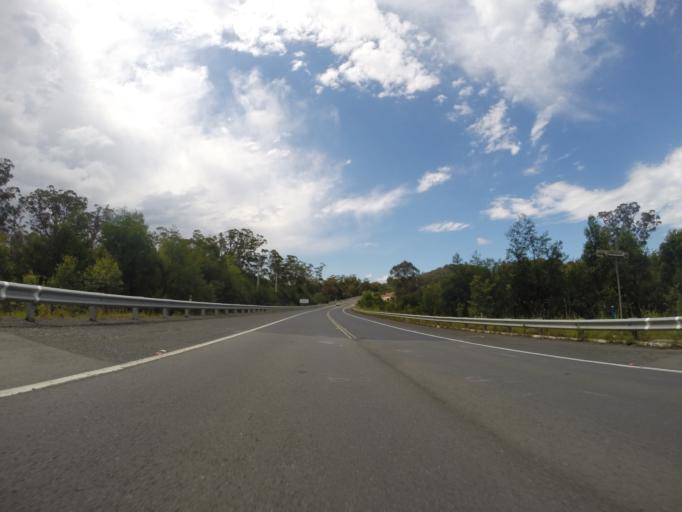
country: AU
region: New South Wales
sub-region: Shoalhaven Shire
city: Milton
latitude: -35.2170
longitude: 150.4348
